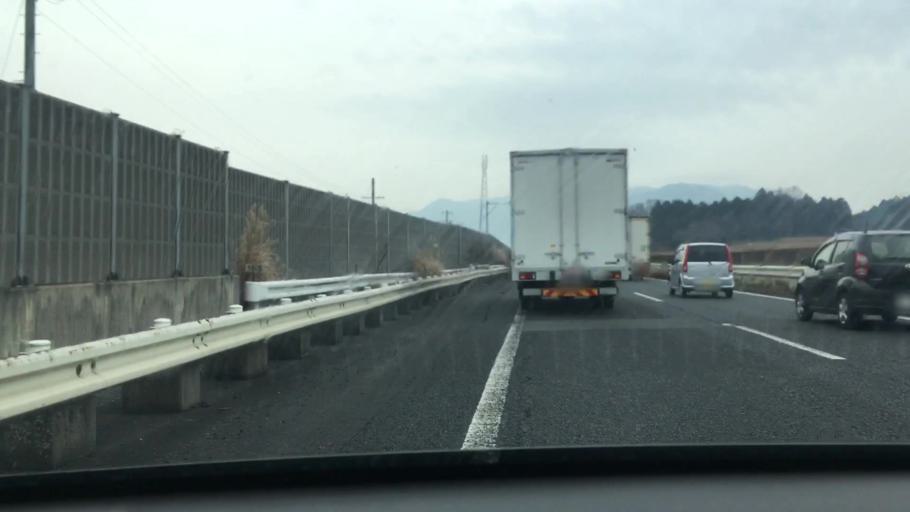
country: JP
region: Mie
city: Ueno-ebisumachi
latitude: 34.8259
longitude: 136.2303
